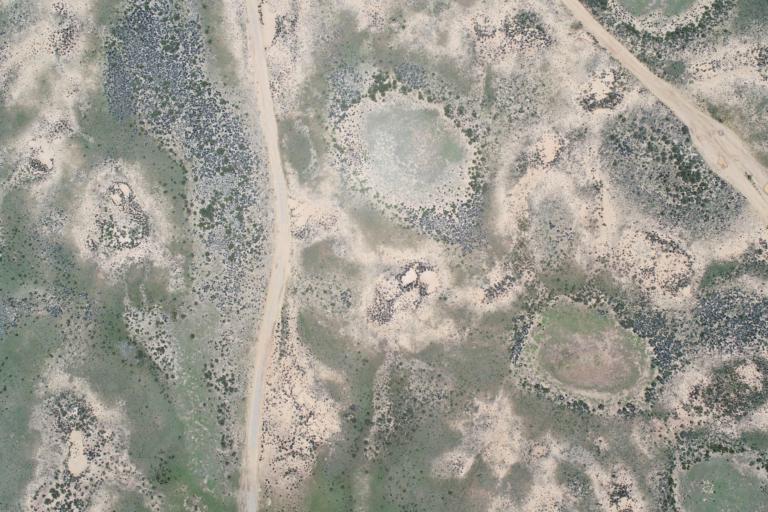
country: BO
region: La Paz
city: Patacamaya
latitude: -17.2808
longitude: -68.5044
